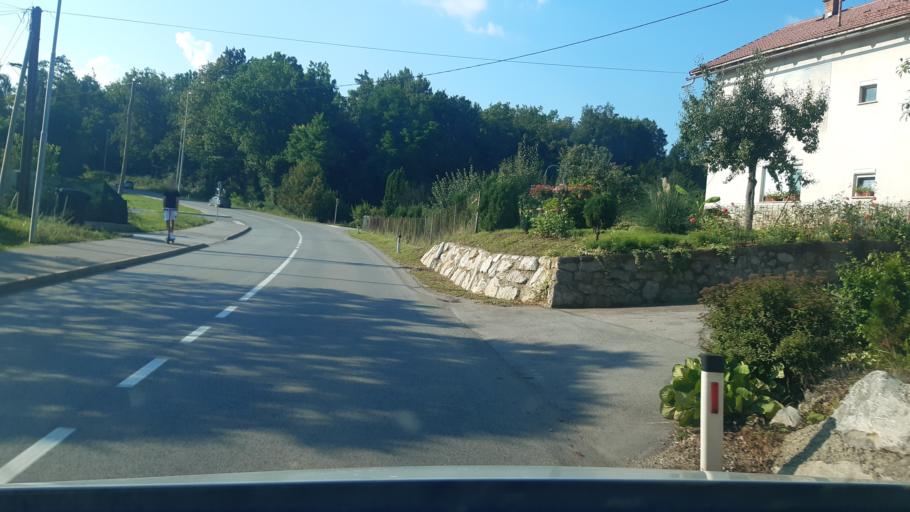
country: SI
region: Crnomelj
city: Crnomelj
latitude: 45.5873
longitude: 15.1822
